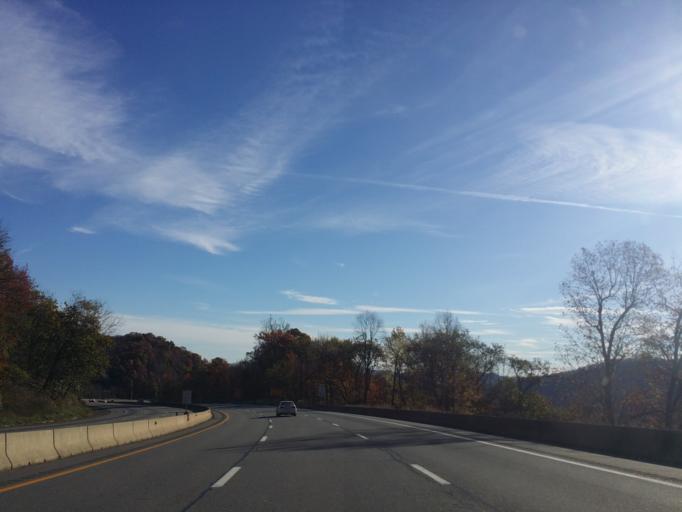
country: US
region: North Carolina
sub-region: Buncombe County
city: Black Mountain
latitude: 35.6220
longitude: -82.2309
